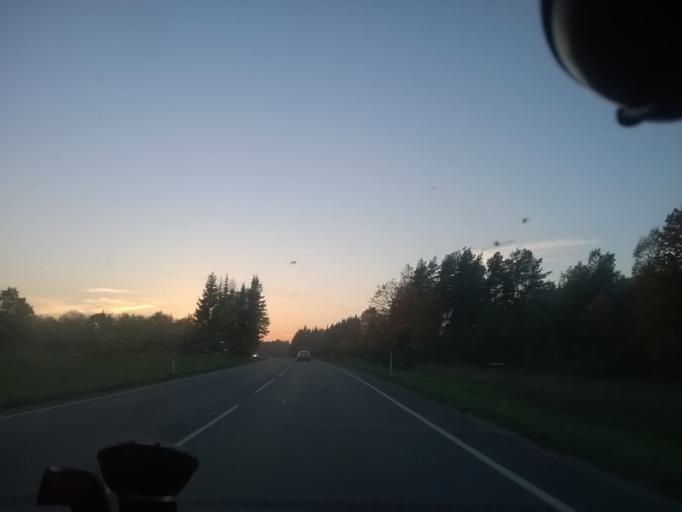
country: EE
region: Laeaene
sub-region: Ridala Parish
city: Uuemoisa
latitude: 58.9614
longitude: 23.6886
